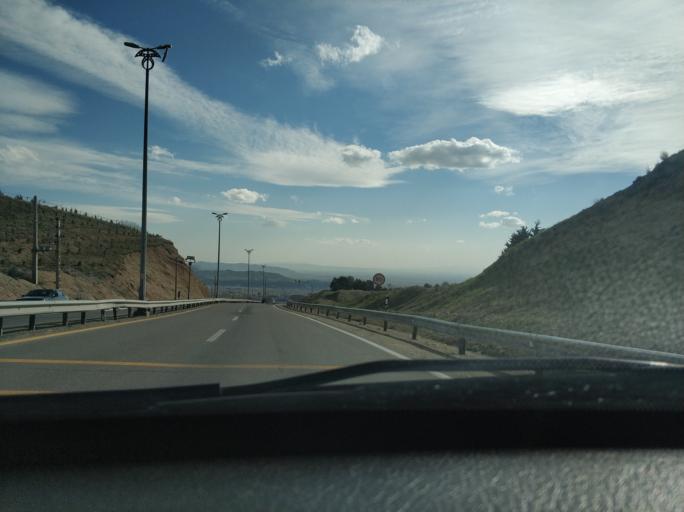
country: IR
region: Tehran
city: Tajrish
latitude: 35.7888
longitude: 51.5672
